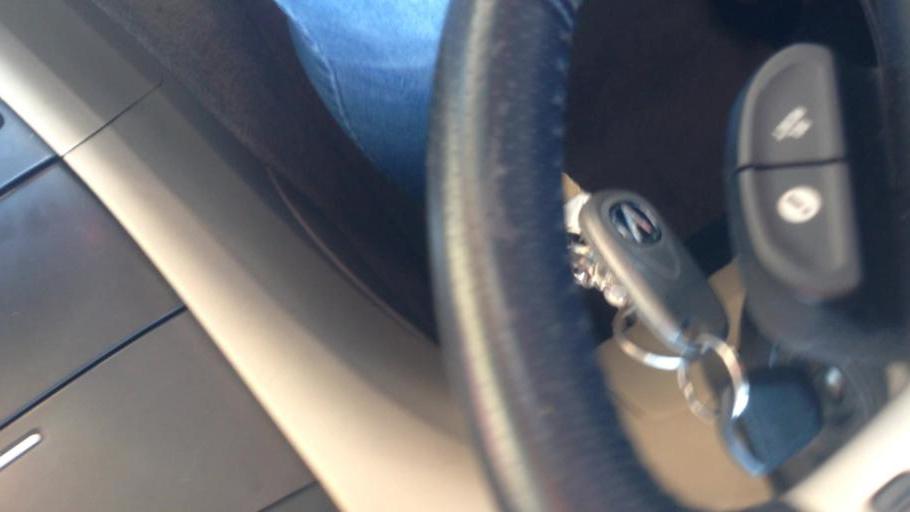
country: US
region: Texas
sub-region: Dallas County
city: Coppell
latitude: 32.9400
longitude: -97.0048
